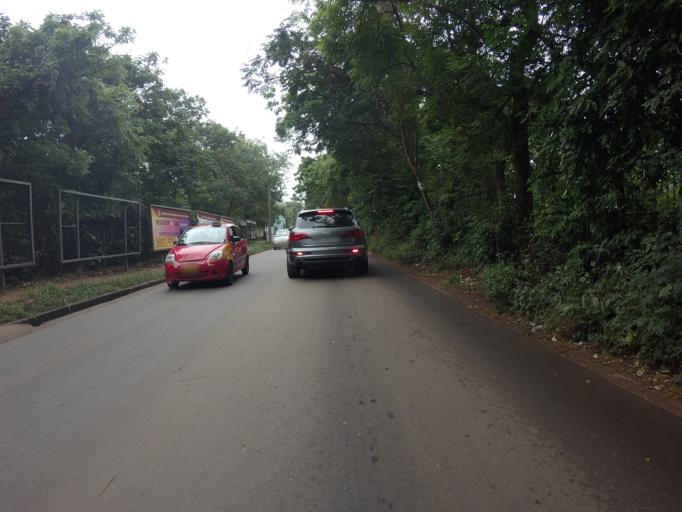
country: GH
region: Greater Accra
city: Dome
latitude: 5.6280
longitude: -0.2197
